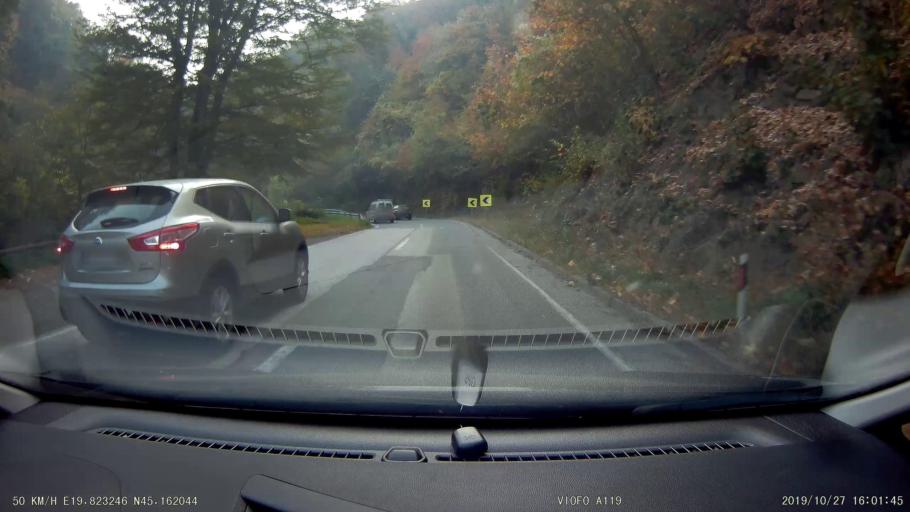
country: RS
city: Vrdnik
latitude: 45.1619
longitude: 19.8231
